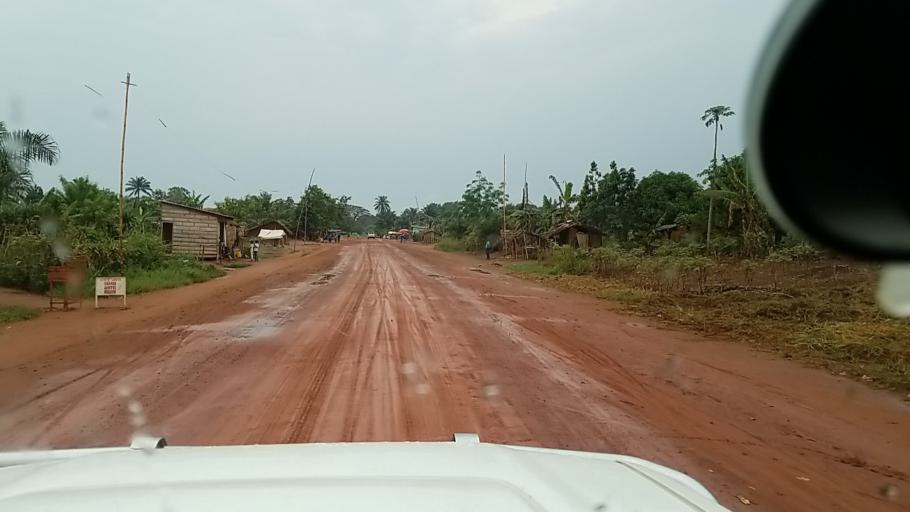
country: CD
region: Equateur
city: Gemena
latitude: 3.2317
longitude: 19.7802
